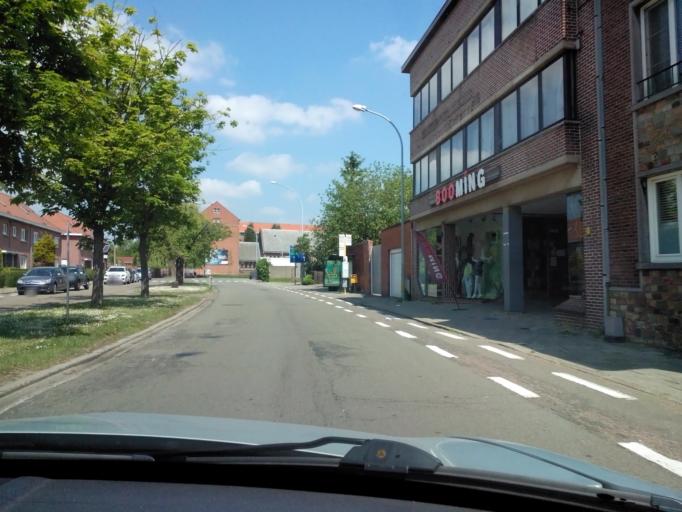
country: BE
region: Flanders
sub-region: Provincie Vlaams-Brabant
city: Aarschot
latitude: 50.9901
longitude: 4.8396
